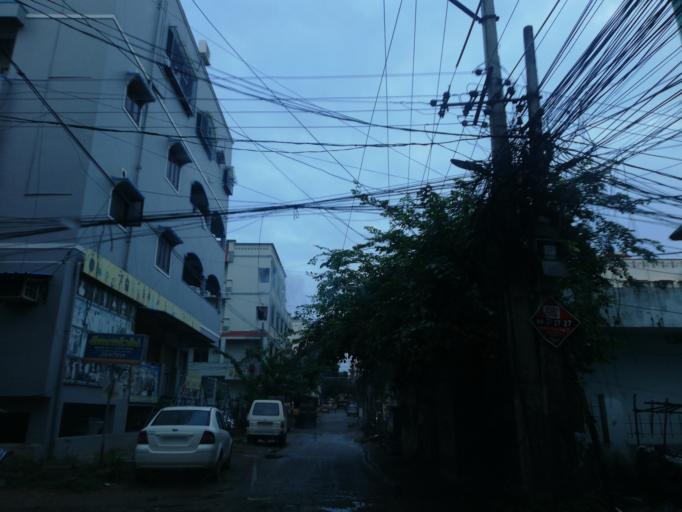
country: IN
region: Telangana
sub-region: Rangareddi
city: Kukatpalli
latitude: 17.4893
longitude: 78.3972
